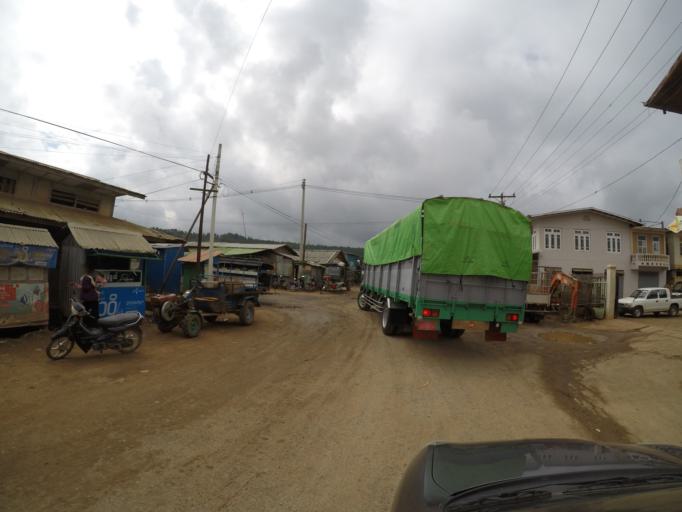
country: MM
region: Shan
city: Taunggyi
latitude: 20.6518
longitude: 96.6315
